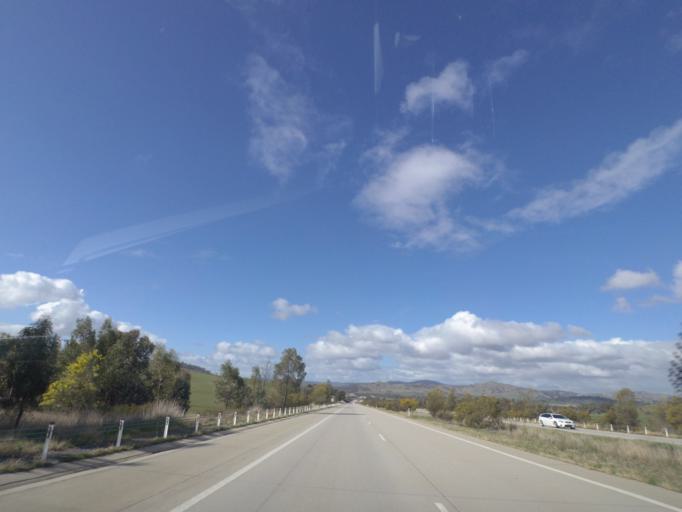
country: AU
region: New South Wales
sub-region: Albury Municipality
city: Lavington
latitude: -35.9153
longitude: 147.1114
